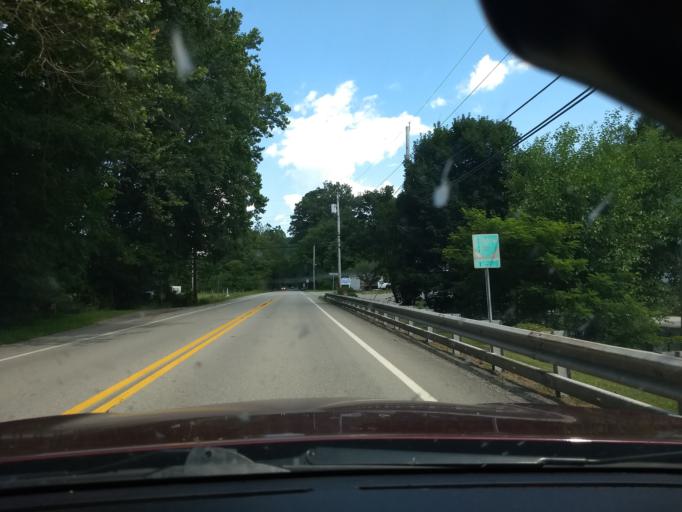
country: US
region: Pennsylvania
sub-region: Westmoreland County
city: Trafford
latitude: 40.3719
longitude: -79.7569
